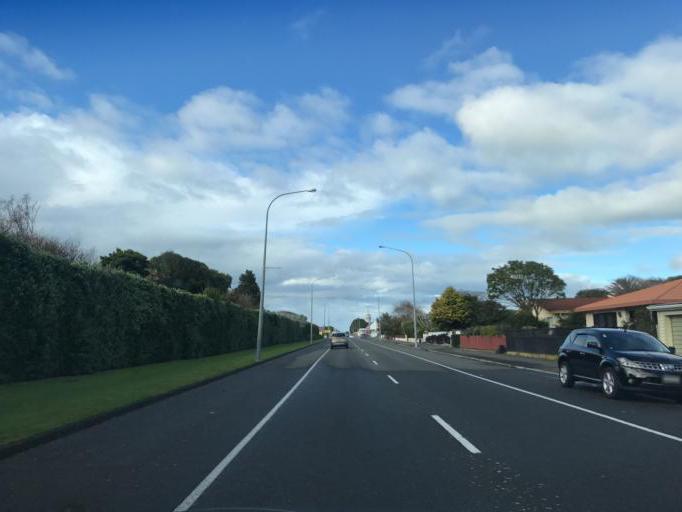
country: NZ
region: Taranaki
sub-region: South Taranaki District
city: Hawera
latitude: -39.5866
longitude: 174.2721
